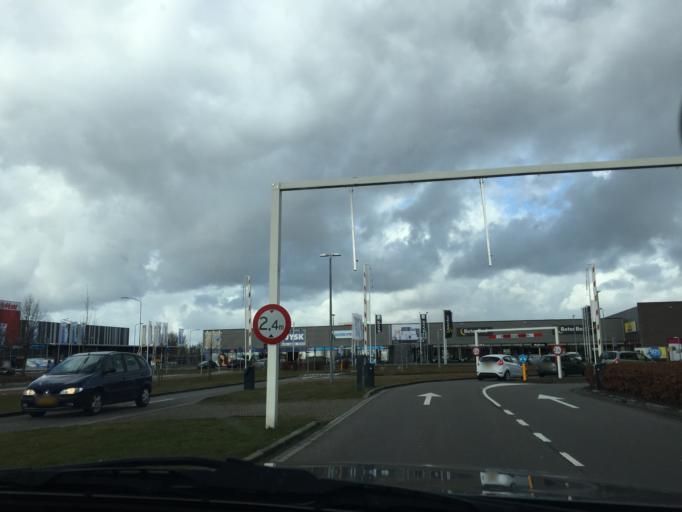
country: NL
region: Gelderland
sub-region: Gemeente Westervoort
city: Westervoort
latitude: 51.9672
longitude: 5.9950
